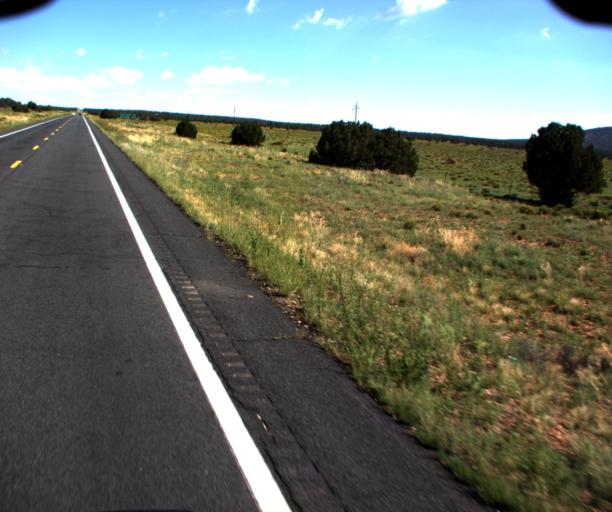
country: US
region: Arizona
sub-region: Coconino County
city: Grand Canyon Village
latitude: 35.7898
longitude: -112.1300
